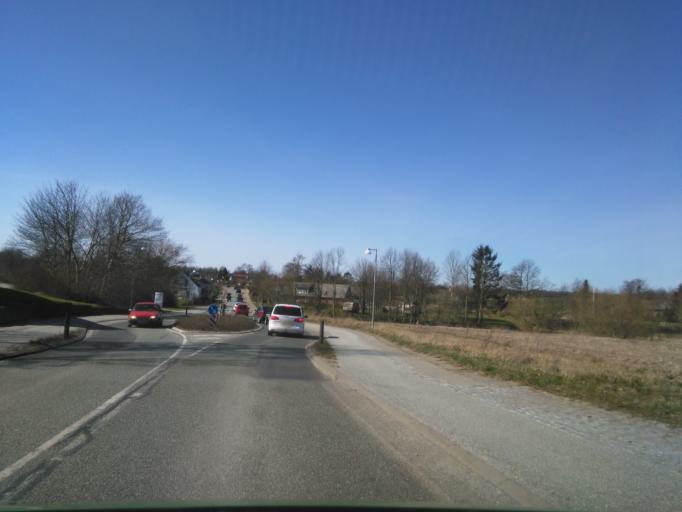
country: DK
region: Central Jutland
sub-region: Favrskov Kommune
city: Hinnerup
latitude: 56.2481
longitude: 10.0375
